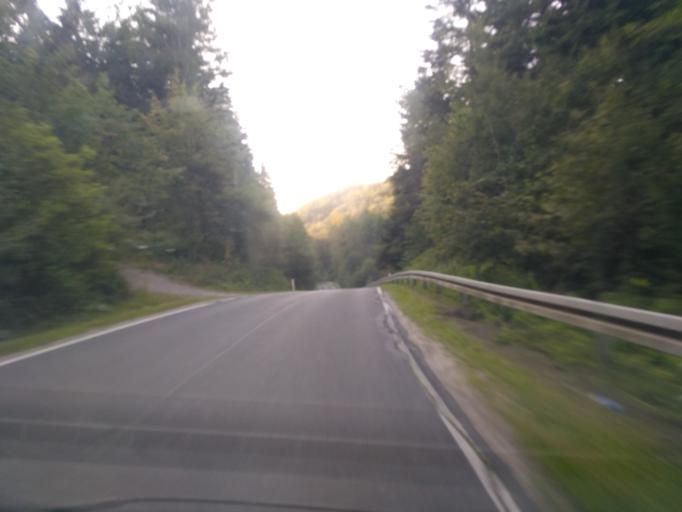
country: PL
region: Subcarpathian Voivodeship
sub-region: Powiat krosnienski
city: Korczyna
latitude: 49.7514
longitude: 21.8003
